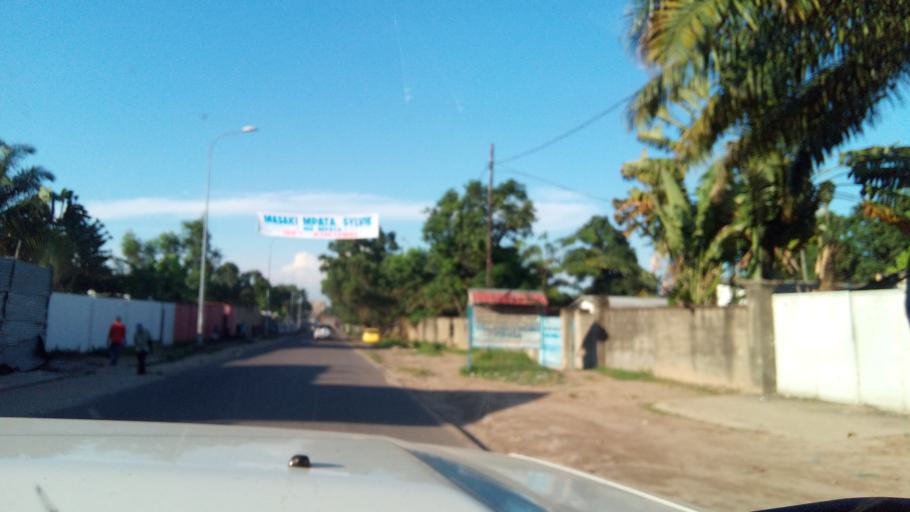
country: CD
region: Kinshasa
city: Kinshasa
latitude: -4.3558
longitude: 15.2633
